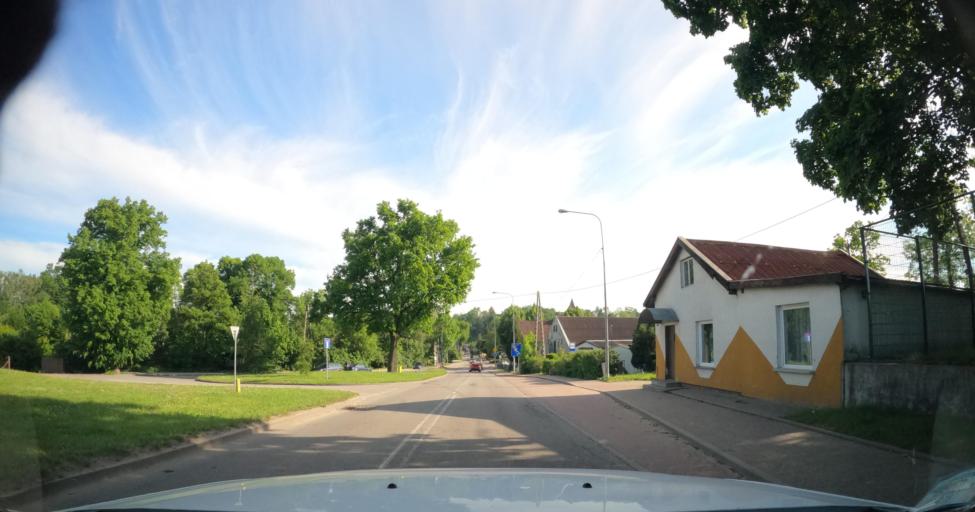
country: PL
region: Warmian-Masurian Voivodeship
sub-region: Powiat elblaski
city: Paslek
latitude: 54.0719
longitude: 19.6608
